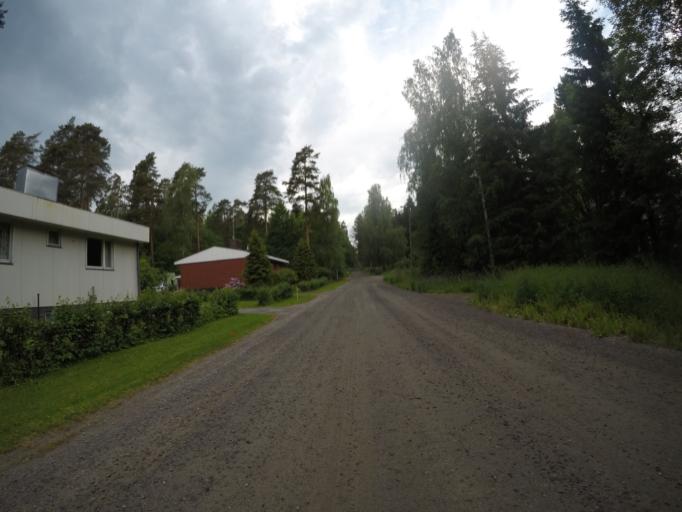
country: FI
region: Haeme
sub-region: Haemeenlinna
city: Haemeenlinna
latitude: 61.0126
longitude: 24.4893
